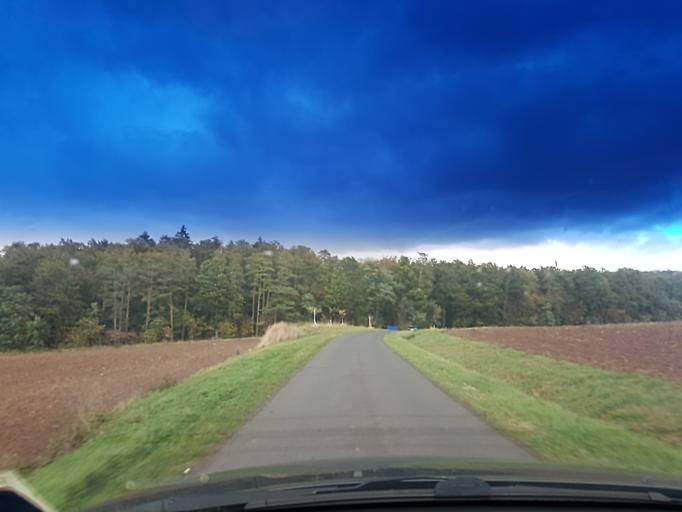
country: DE
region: Bavaria
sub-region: Regierungsbezirk Mittelfranken
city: Burghaslach
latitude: 49.7473
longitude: 10.5843
